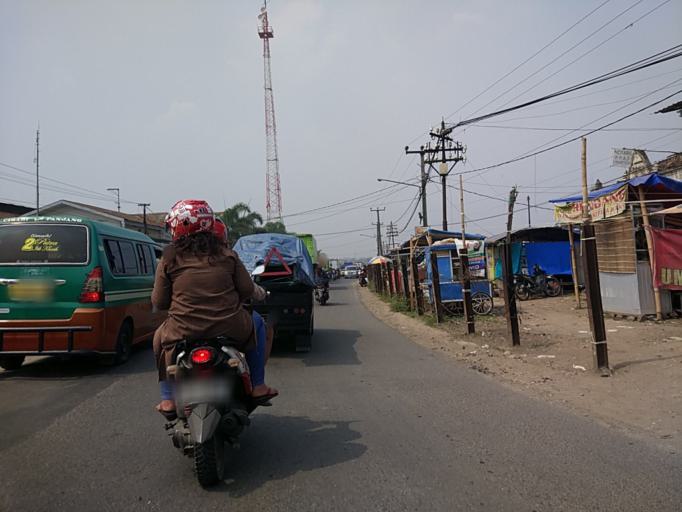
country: ID
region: West Java
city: Padalarang
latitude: -6.8428
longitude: 107.4967
